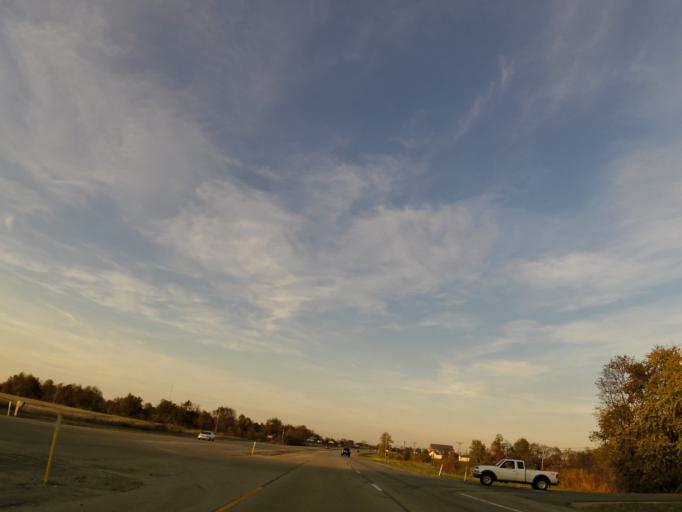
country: US
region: Kentucky
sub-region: Jessamine County
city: Nicholasville
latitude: 37.8152
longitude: -84.5981
